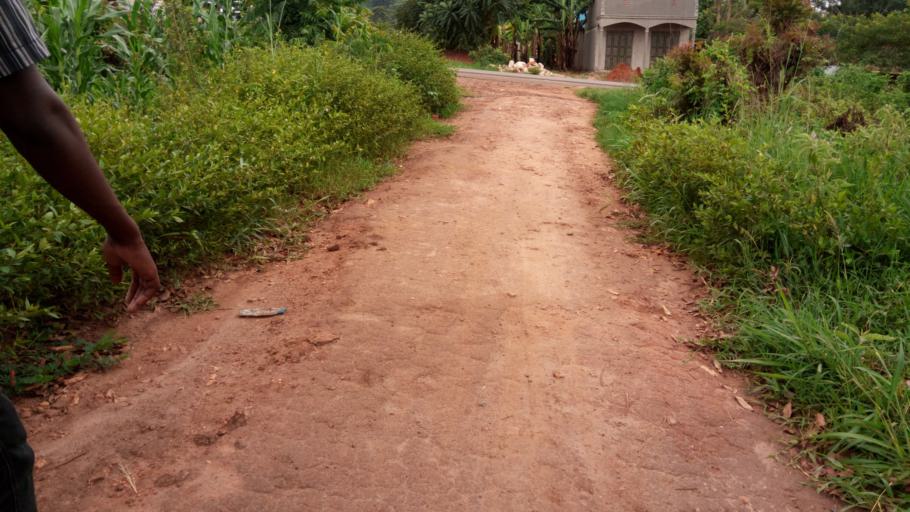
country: UG
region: Central Region
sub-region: Mityana District
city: Mityana
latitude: 0.5699
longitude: 32.1970
